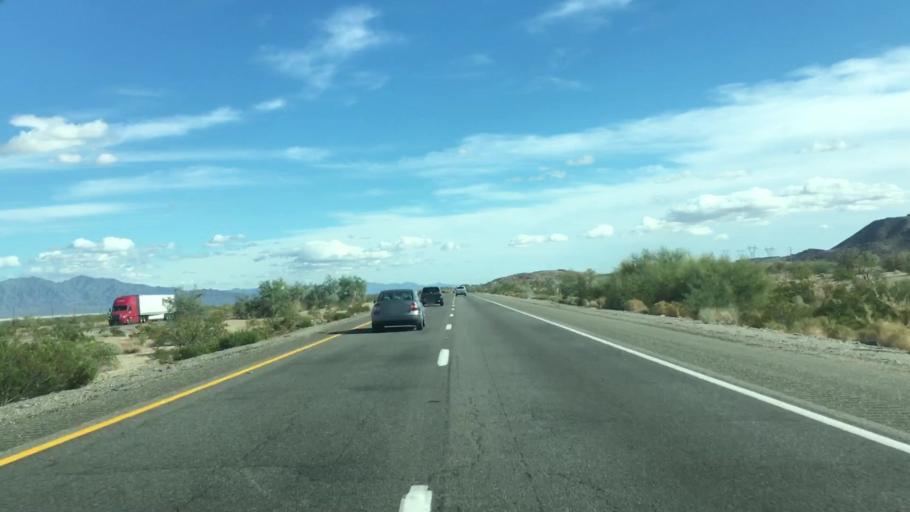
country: US
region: California
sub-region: Imperial County
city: Niland
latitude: 33.7084
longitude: -115.3631
